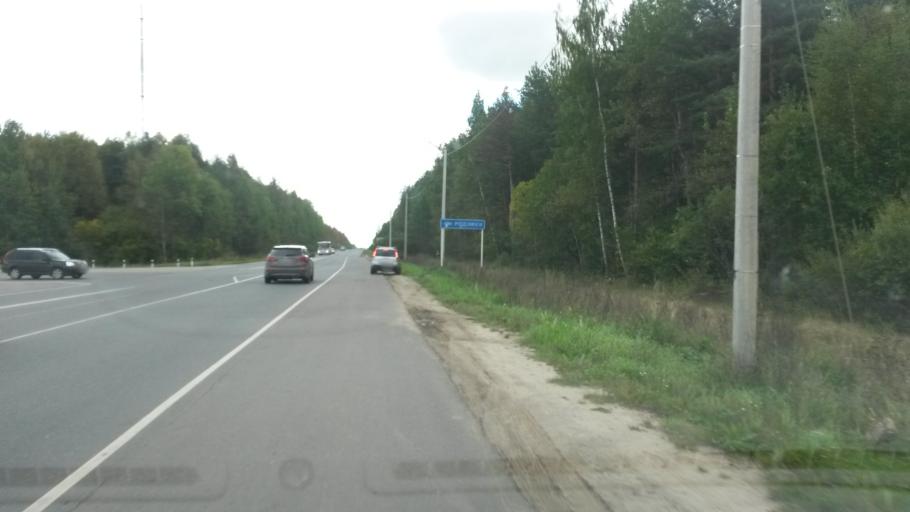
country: RU
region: Ivanovo
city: Rodniki
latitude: 57.0881
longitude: 41.6912
